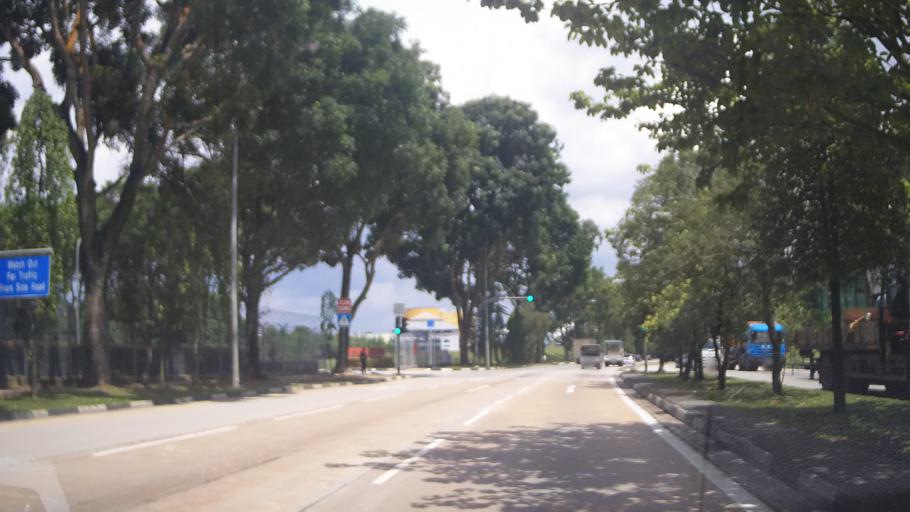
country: MY
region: Johor
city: Johor Bahru
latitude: 1.4023
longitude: 103.7437
